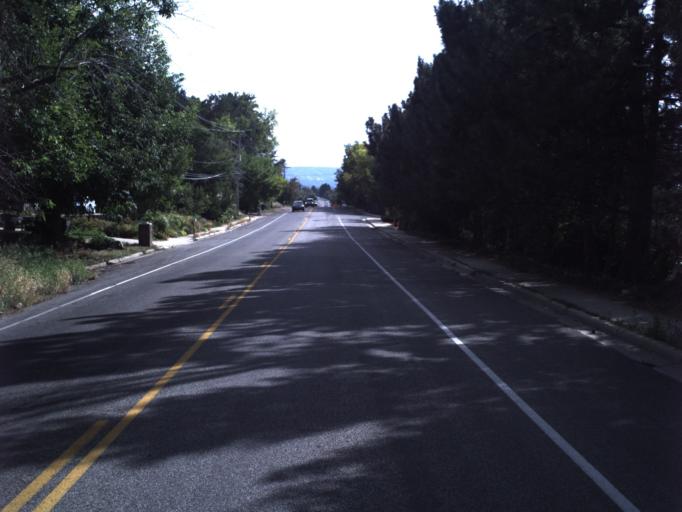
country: US
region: Utah
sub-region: Davis County
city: Farmington
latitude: 40.9612
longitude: -111.8834
